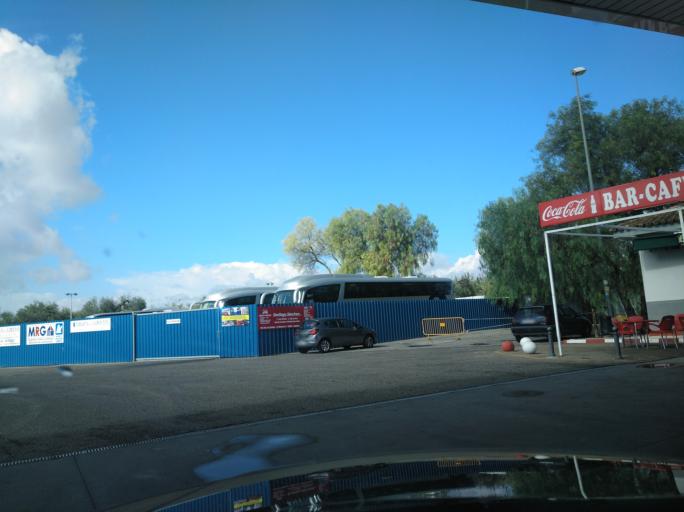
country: ES
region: Andalusia
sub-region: Provincia de Sevilla
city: Umbrete
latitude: 37.3626
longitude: -6.1445
